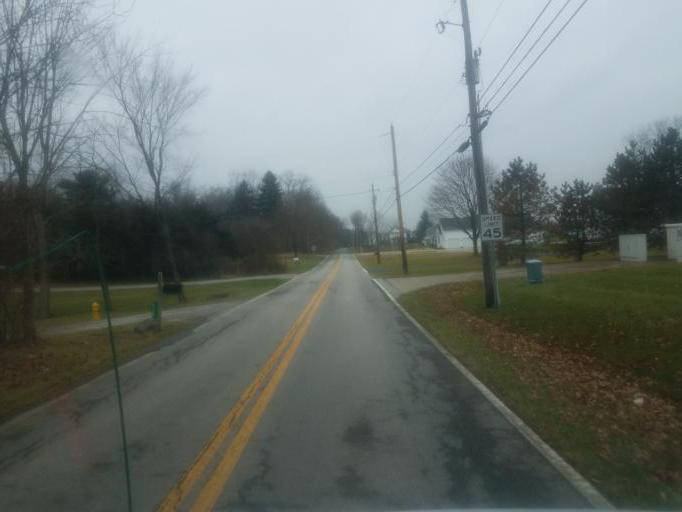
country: US
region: Ohio
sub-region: Franklin County
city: Westerville
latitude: 40.1900
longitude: -82.9266
